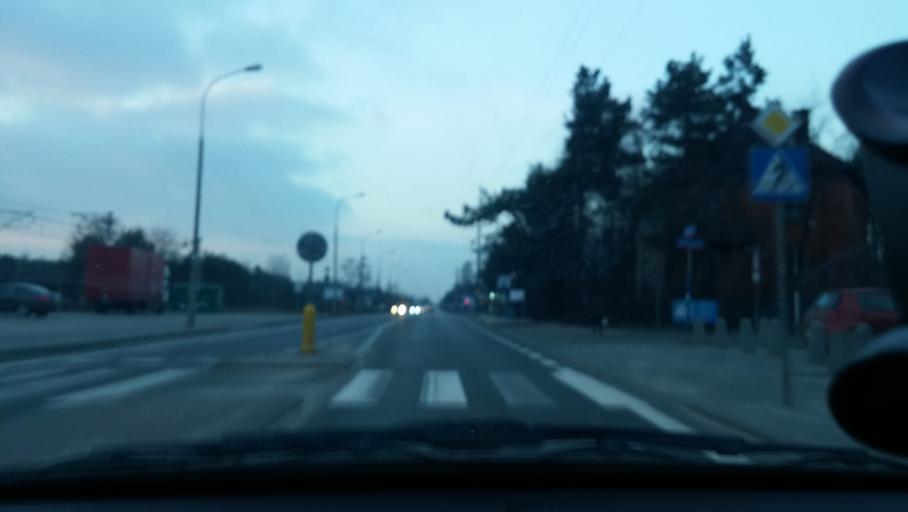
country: PL
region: Masovian Voivodeship
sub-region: Warszawa
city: Wawer
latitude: 52.1920
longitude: 21.1815
